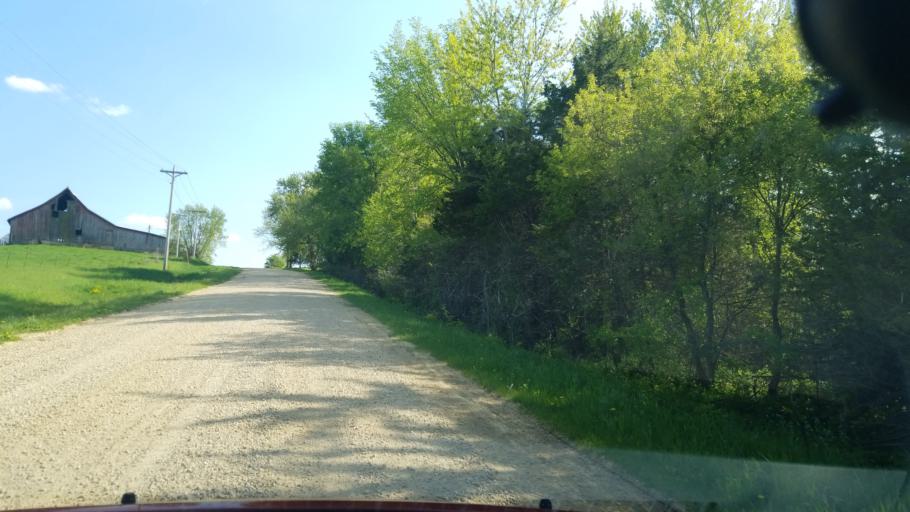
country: US
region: Iowa
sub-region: Jackson County
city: Maquoketa
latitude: 42.2085
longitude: -90.7298
